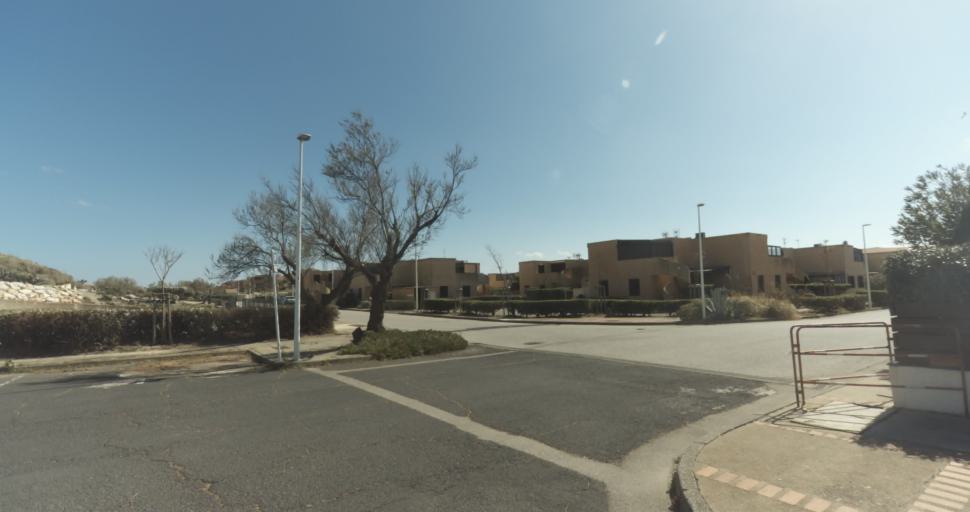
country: FR
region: Languedoc-Roussillon
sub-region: Departement de l'Aude
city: Leucate
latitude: 42.8539
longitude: 3.0421
